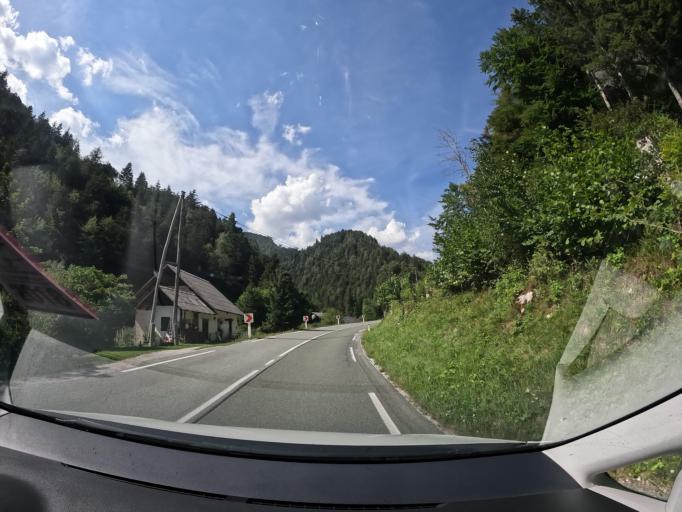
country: SI
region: Preddvor
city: Preddvor
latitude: 46.3643
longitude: 14.4282
